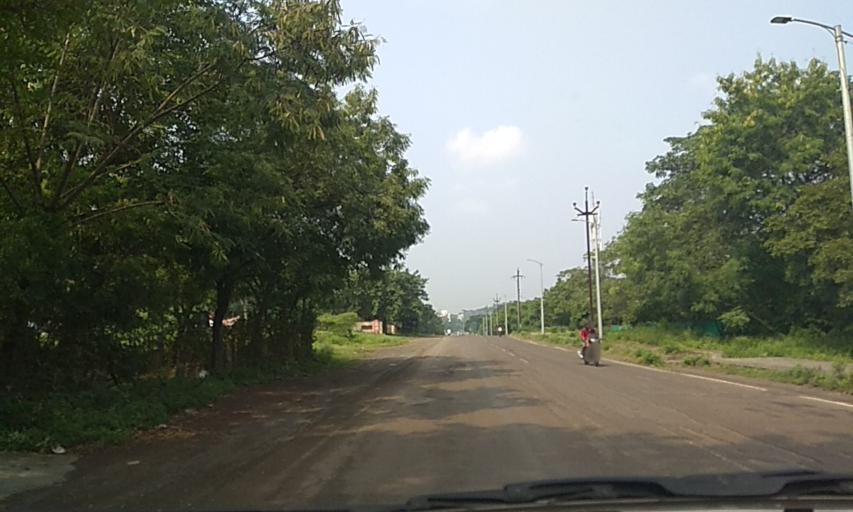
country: IN
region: Maharashtra
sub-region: Pune Division
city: Shivaji Nagar
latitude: 18.5450
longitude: 73.8459
